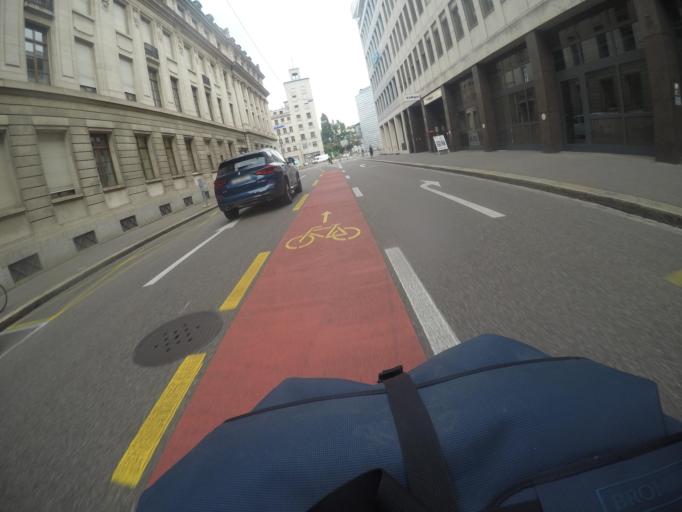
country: CH
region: Basel-City
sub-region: Basel-Stadt
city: Basel
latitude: 47.5523
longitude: 7.5952
